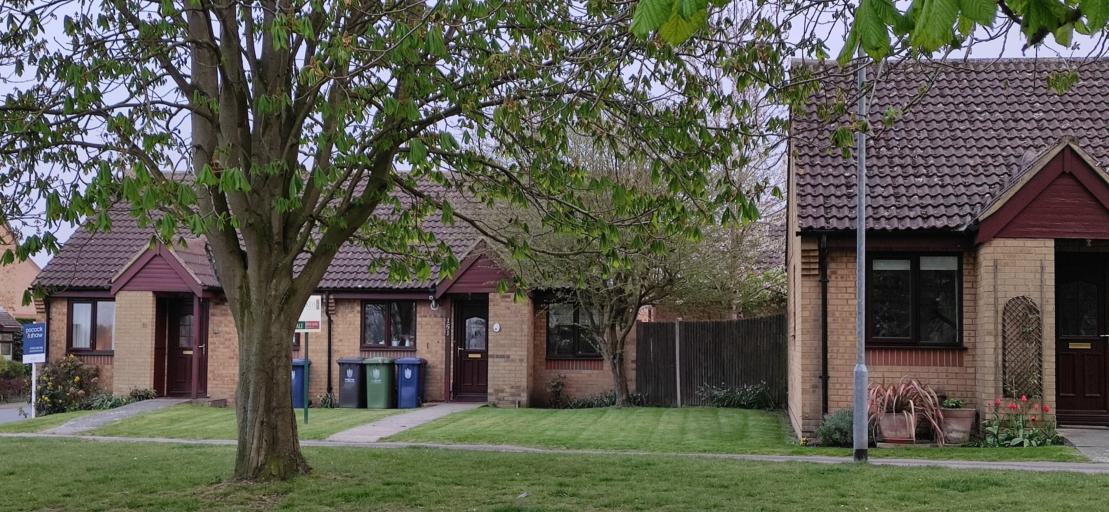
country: GB
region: England
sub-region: Cambridgeshire
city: Swavesey
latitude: 52.2510
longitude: 0.0169
